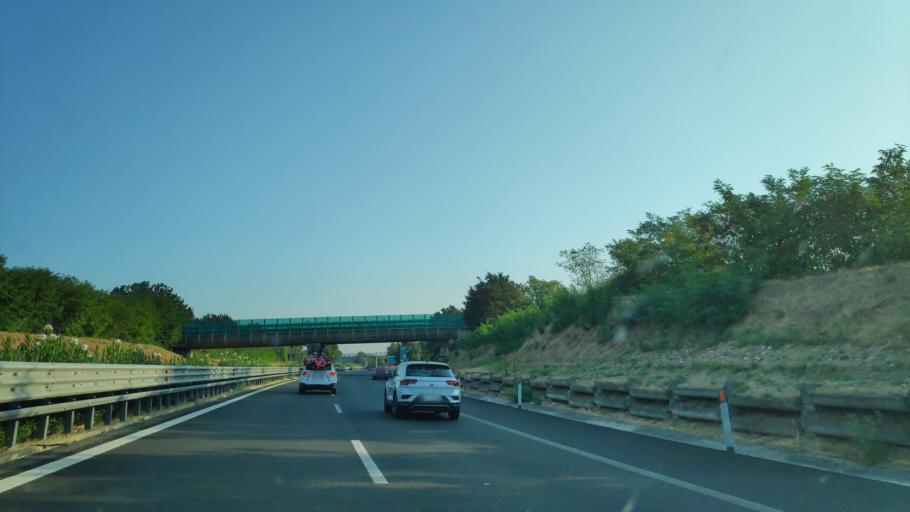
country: IT
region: Calabria
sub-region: Provincia di Cosenza
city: Quattromiglia
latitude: 39.3416
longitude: 16.2346
